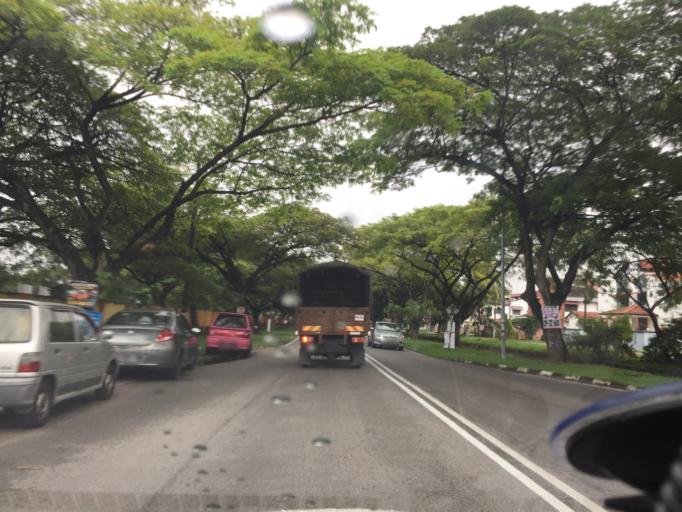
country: MY
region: Selangor
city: Klang
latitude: 3.0098
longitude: 101.4481
